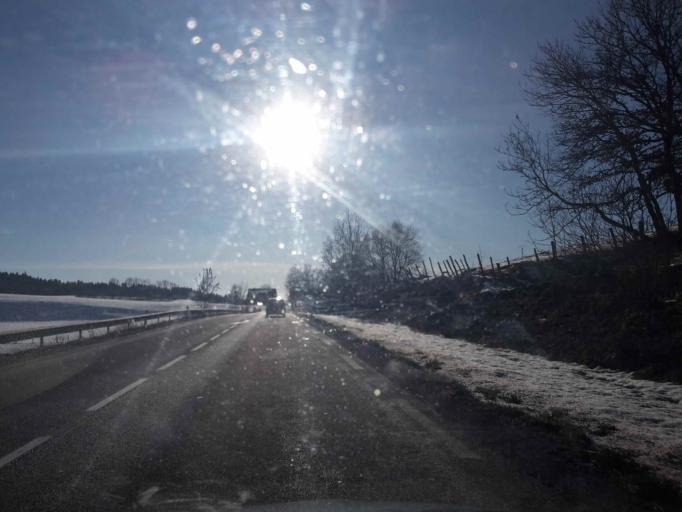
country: FR
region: Franche-Comte
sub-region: Departement du Doubs
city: Doubs
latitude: 47.0370
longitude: 6.3387
